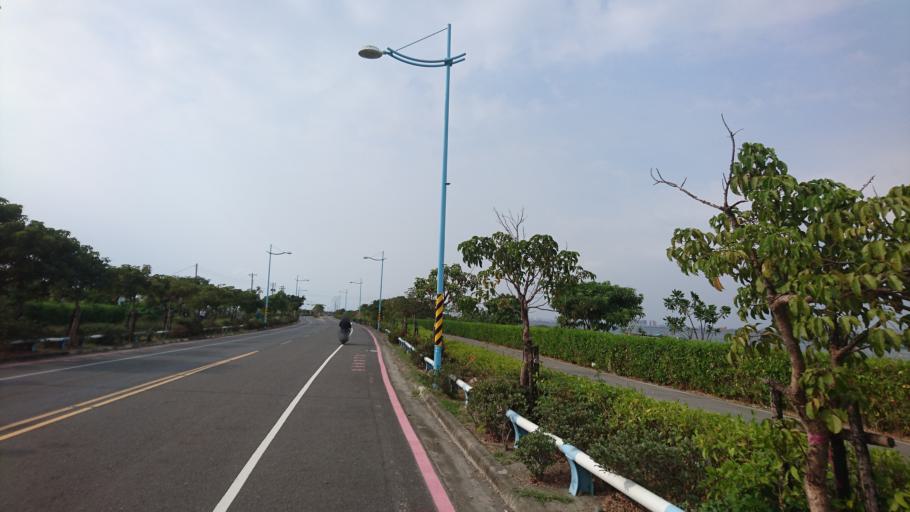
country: TW
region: Taiwan
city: Fengshan
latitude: 22.4320
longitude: 120.4859
